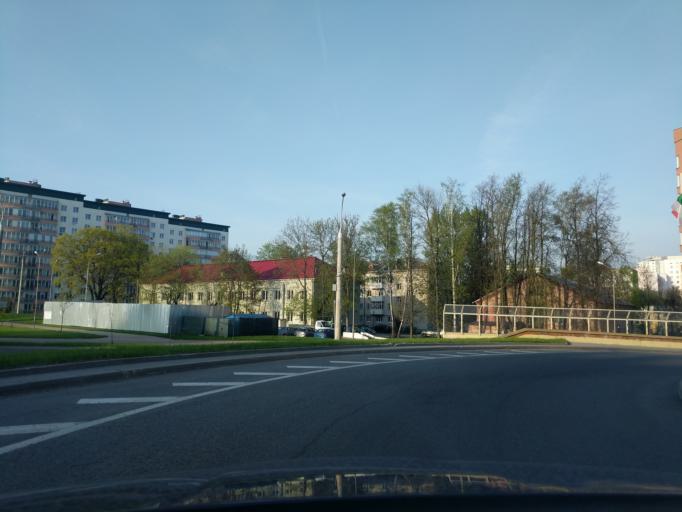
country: BY
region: Minsk
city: Minsk
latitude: 53.8735
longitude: 27.5702
